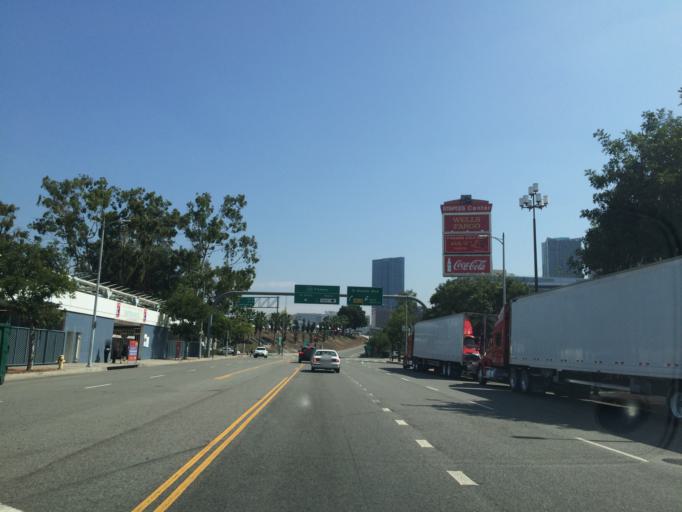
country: US
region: California
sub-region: Los Angeles County
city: Los Angeles
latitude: 34.0441
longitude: -118.2707
